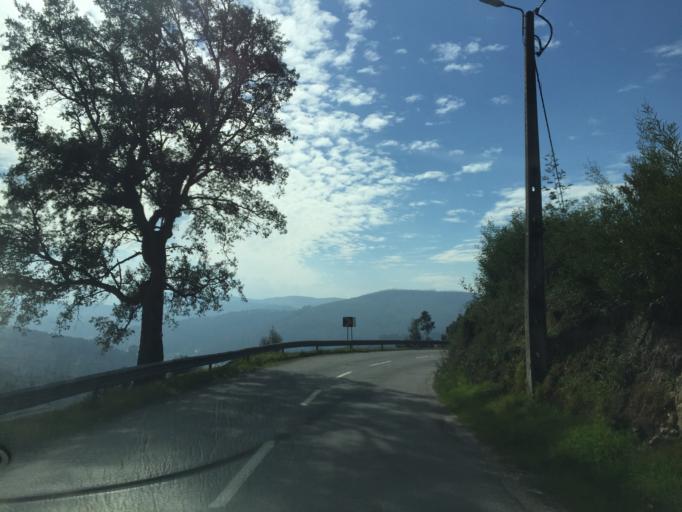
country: PT
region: Aveiro
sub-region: Castelo de Paiva
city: Castelo de Paiva
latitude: 41.0337
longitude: -8.2665
